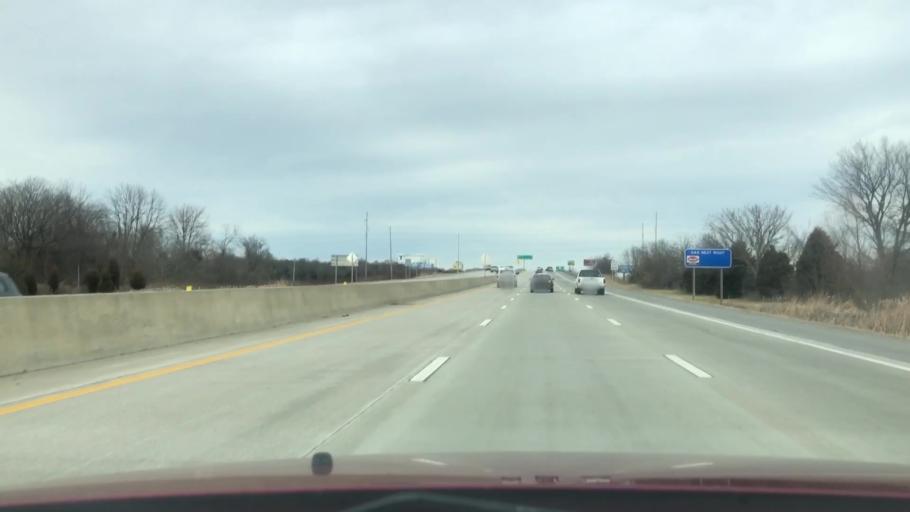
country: US
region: Missouri
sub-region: Greene County
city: Springfield
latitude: 37.2293
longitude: -93.2250
